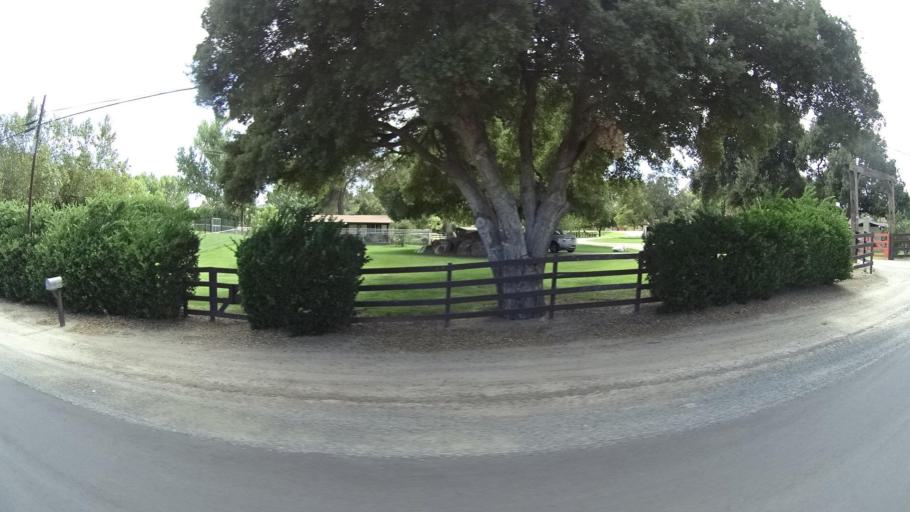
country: MX
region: Baja California
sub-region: Tecate
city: Cereso del Hongo
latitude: 32.6467
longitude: -116.2879
